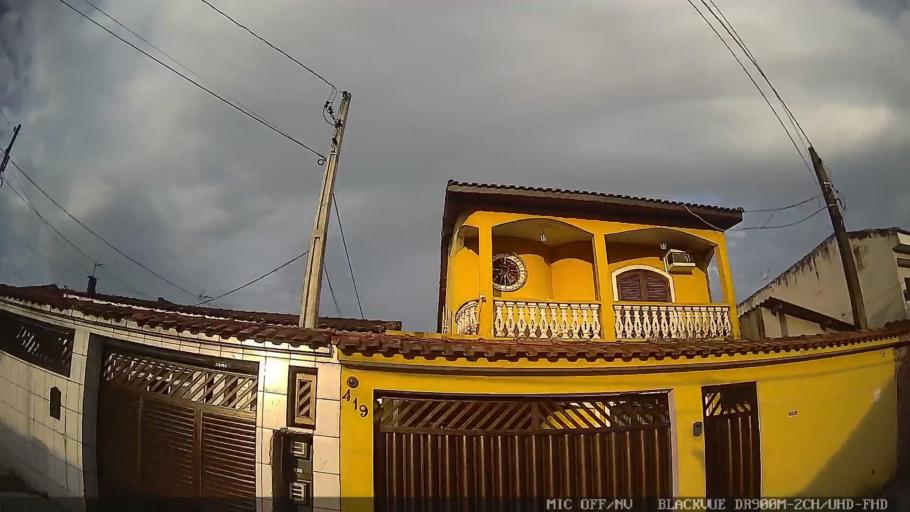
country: BR
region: Sao Paulo
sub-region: Cubatao
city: Cubatao
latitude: -23.8959
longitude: -46.4279
